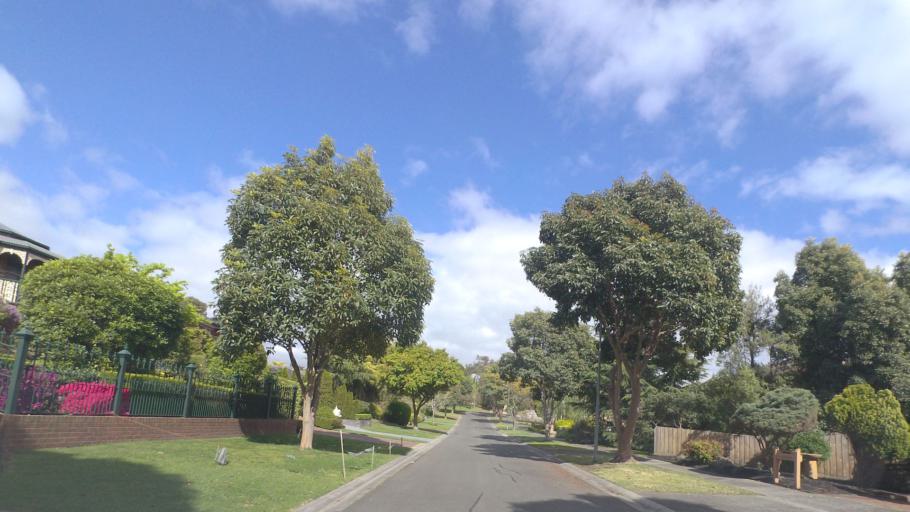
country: AU
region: Victoria
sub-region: Maroondah
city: Croydon South
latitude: -37.8036
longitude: 145.2678
